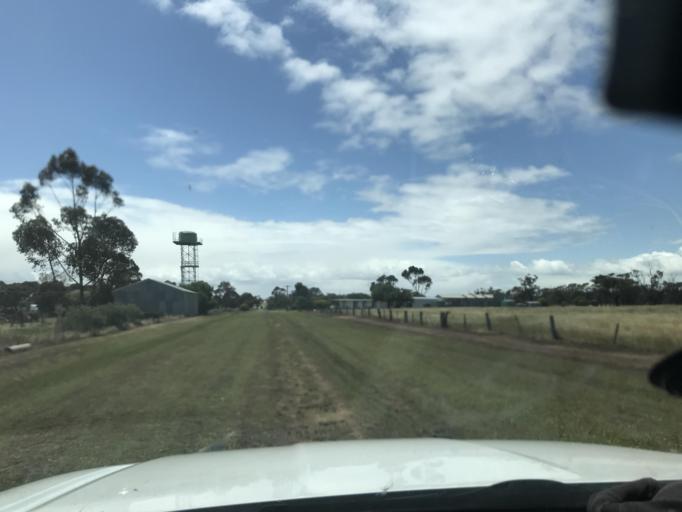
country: AU
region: South Australia
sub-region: Tatiara
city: Bordertown
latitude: -36.3631
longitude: 141.1248
